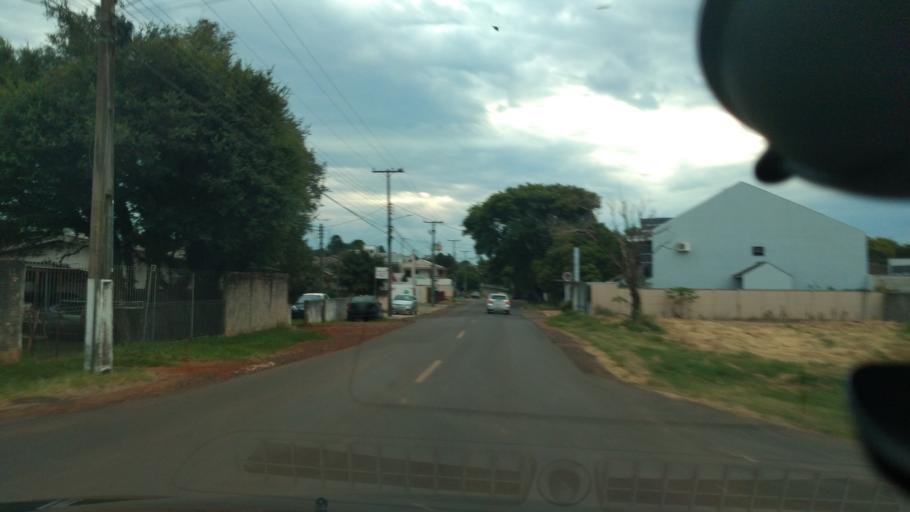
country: BR
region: Parana
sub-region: Guarapuava
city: Guarapuava
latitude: -25.3887
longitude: -51.4835
